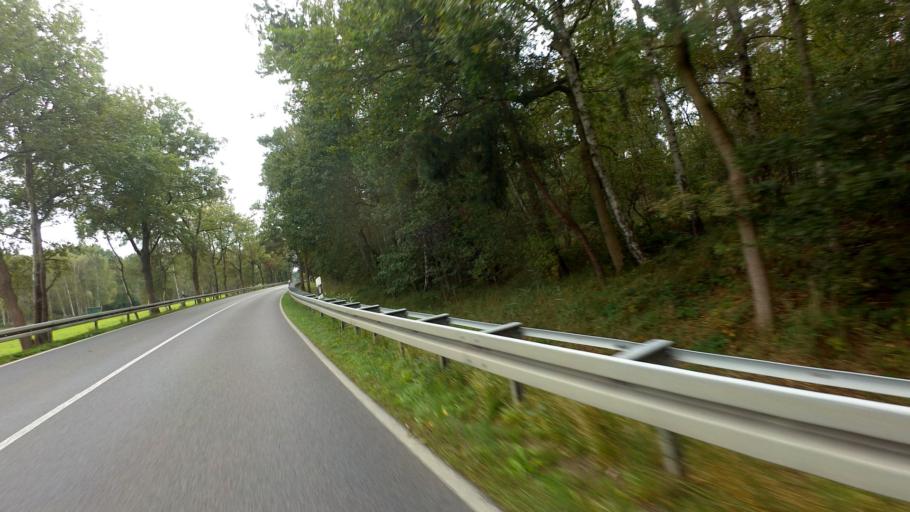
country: DE
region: Brandenburg
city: Luckau
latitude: 51.7931
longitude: 13.6892
